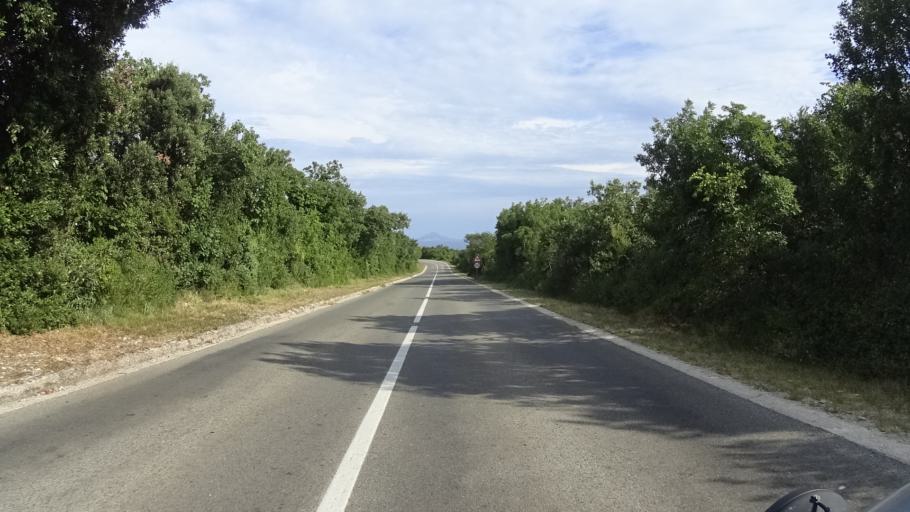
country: HR
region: Istarska
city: Rasa
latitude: 44.9954
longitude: 14.1052
